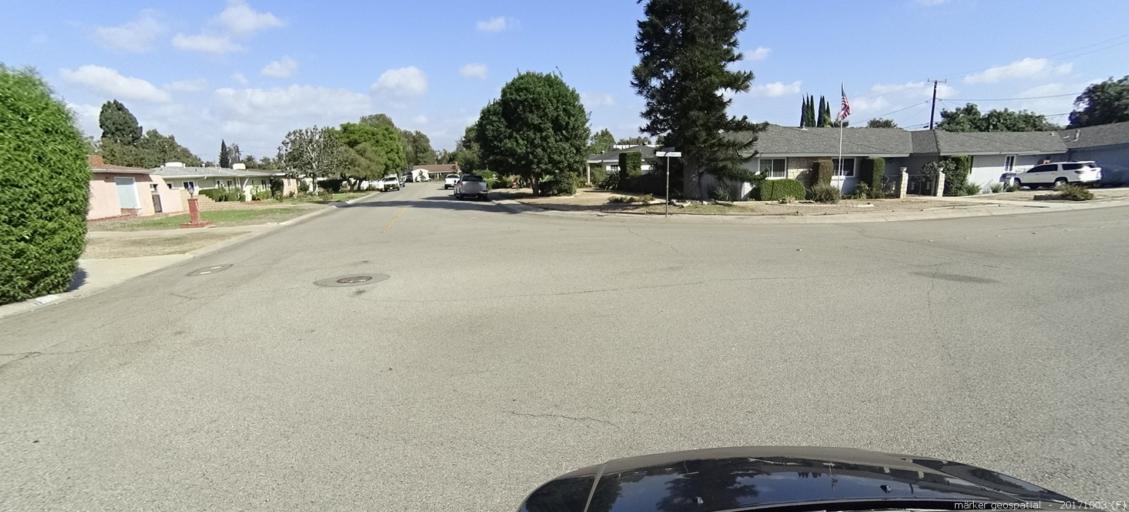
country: US
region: California
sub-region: Orange County
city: Garden Grove
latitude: 33.7752
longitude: -117.9698
